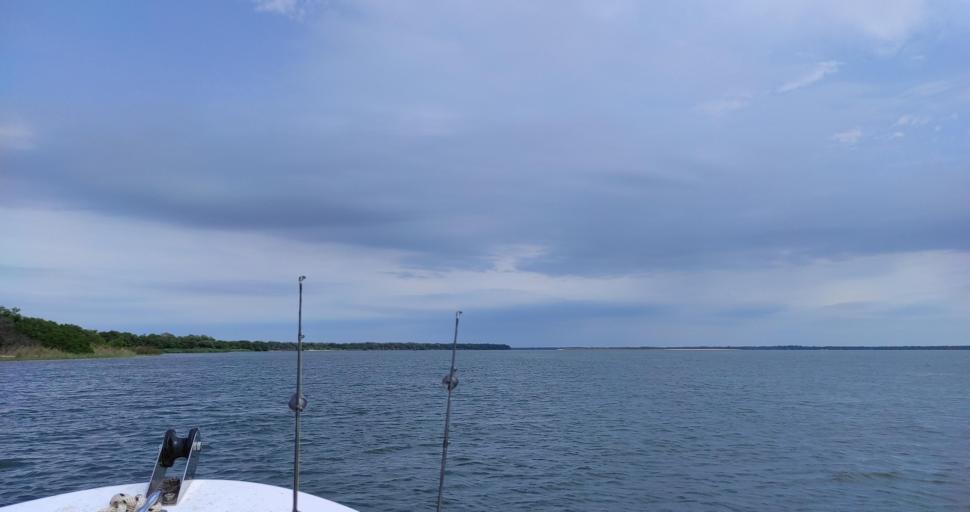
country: PY
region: Neembucu
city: Cerrito
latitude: -27.3462
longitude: -57.6870
